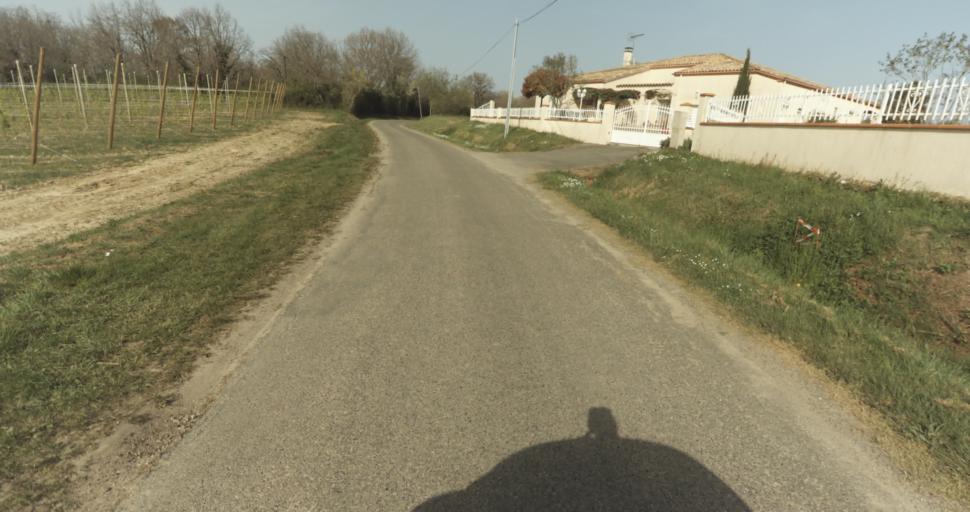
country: FR
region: Midi-Pyrenees
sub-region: Departement du Tarn-et-Garonne
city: Moissac
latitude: 44.1255
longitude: 1.1641
